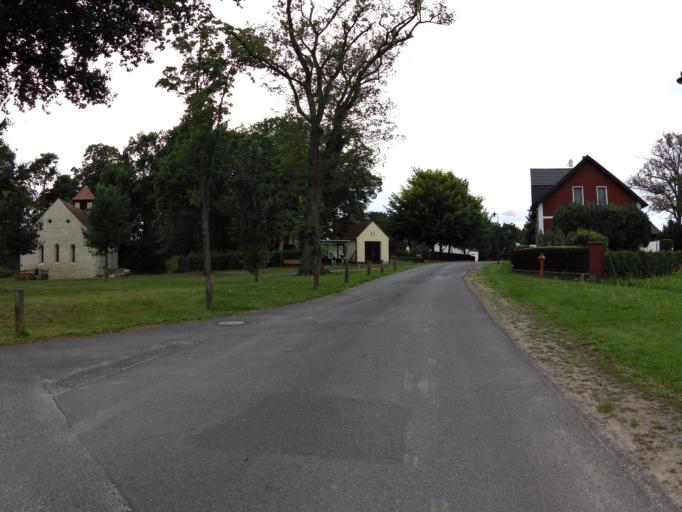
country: DE
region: Brandenburg
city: Reichenwalde
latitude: 52.2356
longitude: 13.9910
